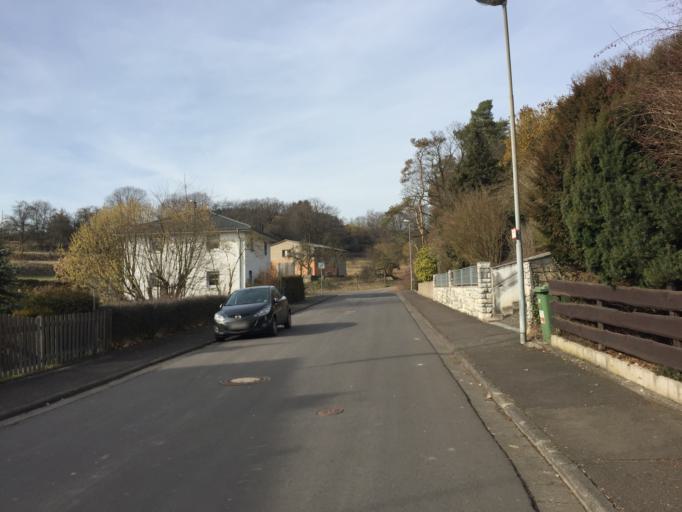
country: DE
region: Hesse
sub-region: Regierungsbezirk Giessen
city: Fronhausen
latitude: 50.6857
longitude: 8.6845
